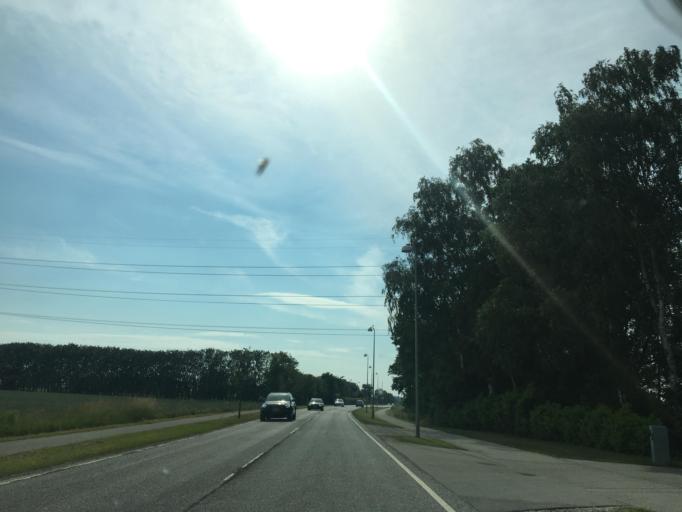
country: DK
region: Zealand
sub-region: Greve Kommune
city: Tune
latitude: 55.5972
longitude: 12.2088
